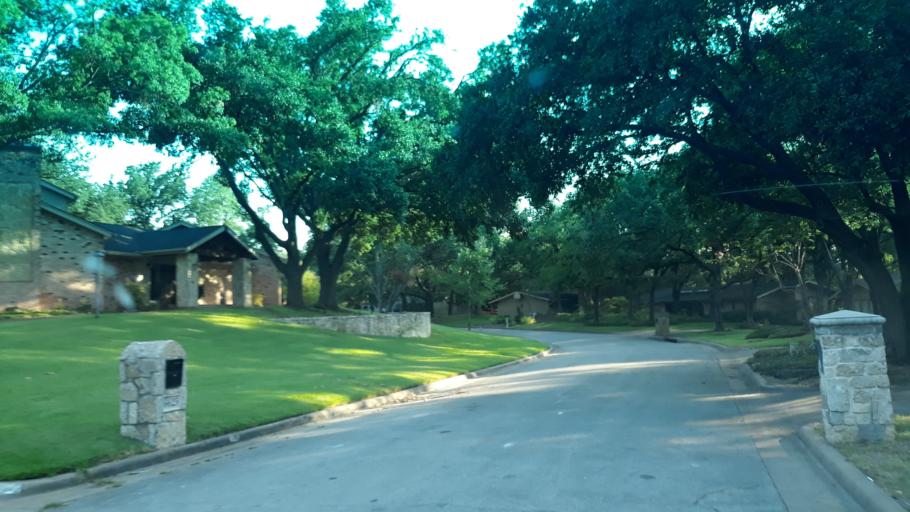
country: US
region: Texas
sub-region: Dallas County
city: Addison
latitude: 32.9457
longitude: -96.7890
